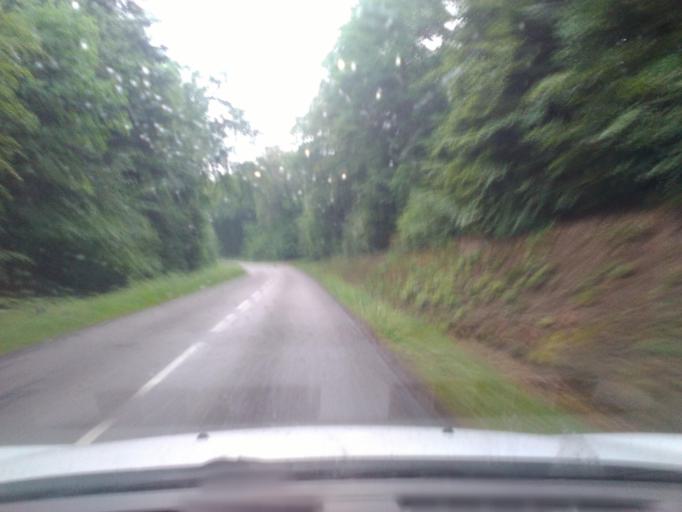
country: FR
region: Lorraine
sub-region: Departement des Vosges
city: Jeanmenil
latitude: 48.2833
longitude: 6.7026
